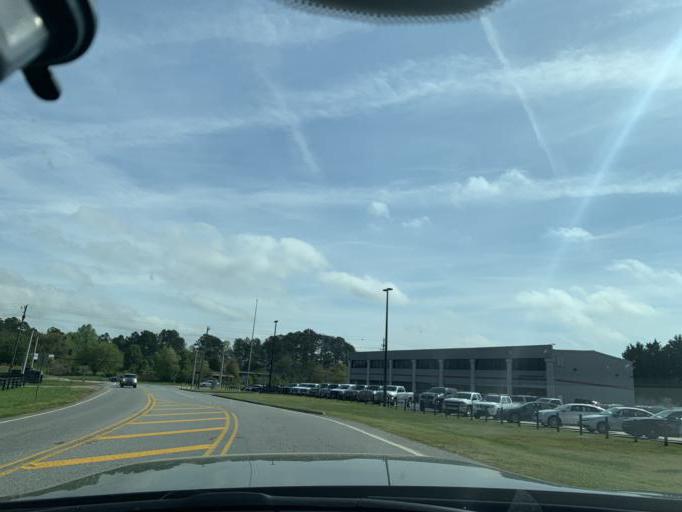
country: US
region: Georgia
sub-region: Forsyth County
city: Cumming
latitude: 34.2535
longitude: -84.0695
